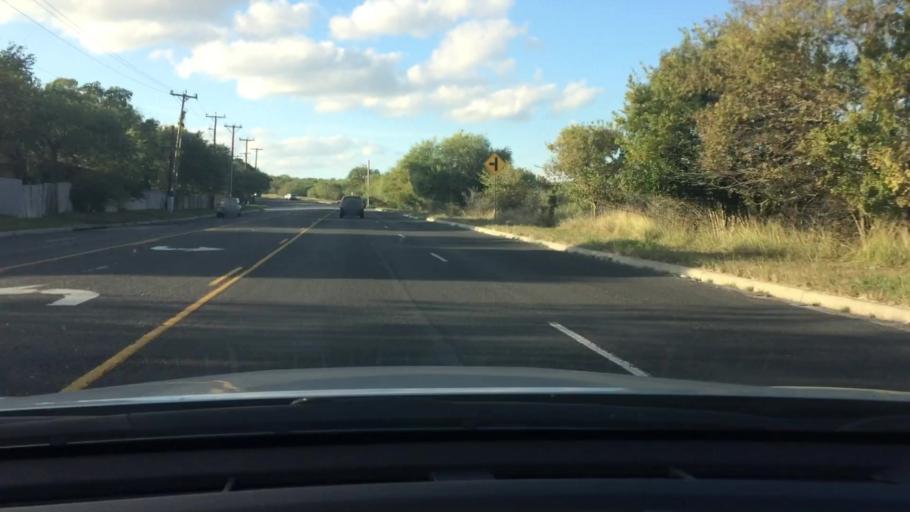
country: US
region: Texas
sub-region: Bexar County
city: Converse
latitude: 29.5165
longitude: -98.3301
